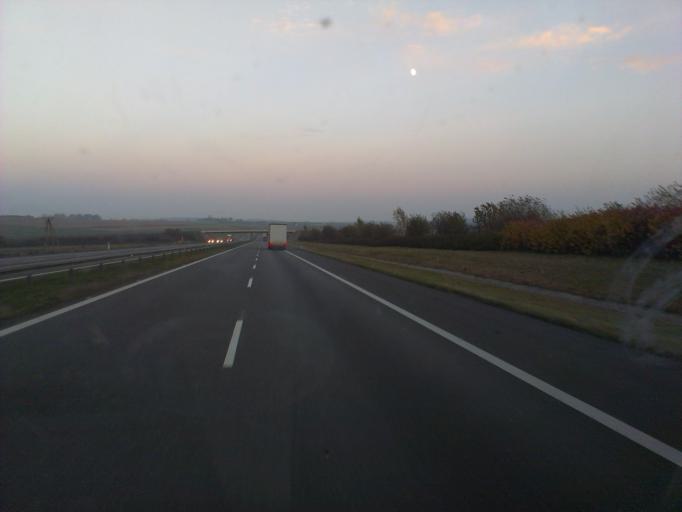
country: PL
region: Opole Voivodeship
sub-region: Powiat strzelecki
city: Lesnica
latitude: 50.4663
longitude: 18.2009
